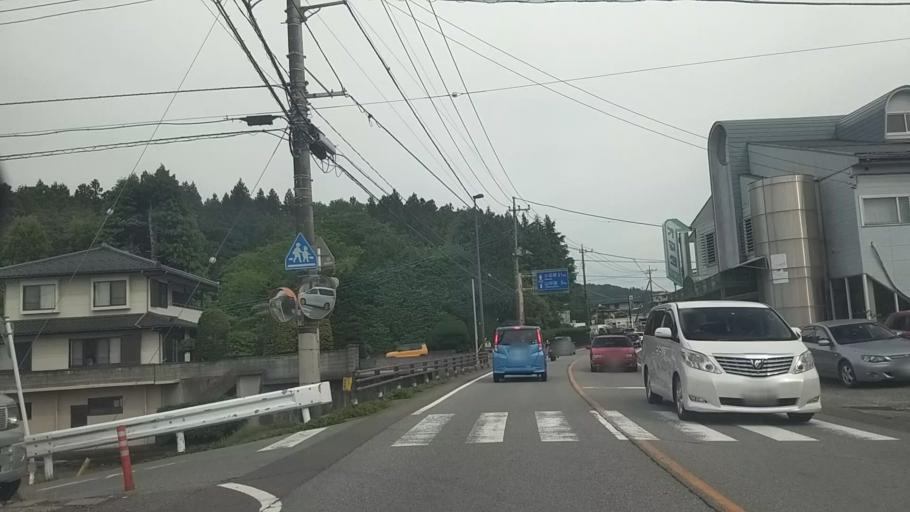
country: JP
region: Yamanashi
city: Fujikawaguchiko
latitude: 35.4699
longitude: 138.8001
